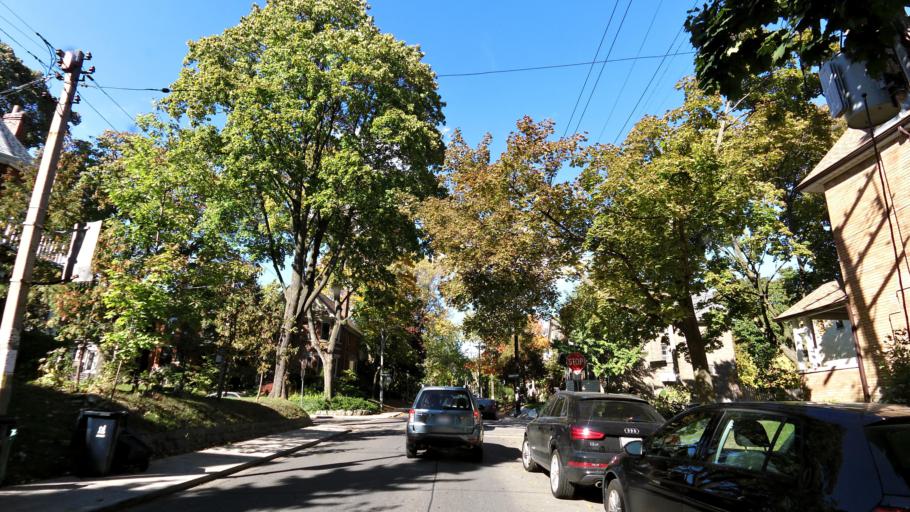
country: CA
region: Ontario
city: Toronto
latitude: 43.6448
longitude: -79.4509
